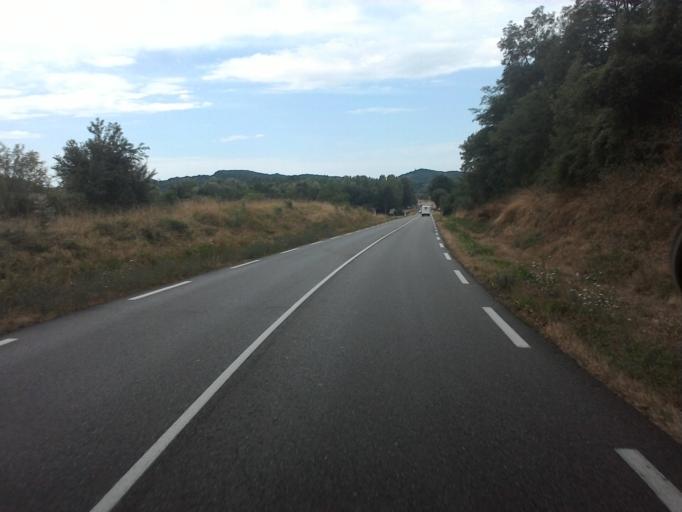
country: FR
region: Franche-Comte
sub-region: Departement du Jura
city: Poligny
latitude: 46.8170
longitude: 5.5926
